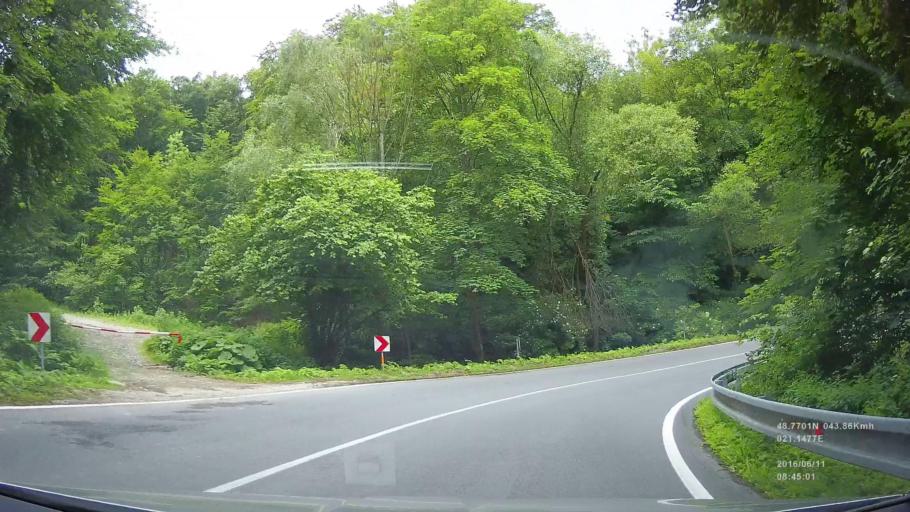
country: SK
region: Kosicky
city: Kosice
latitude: 48.7554
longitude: 21.1957
